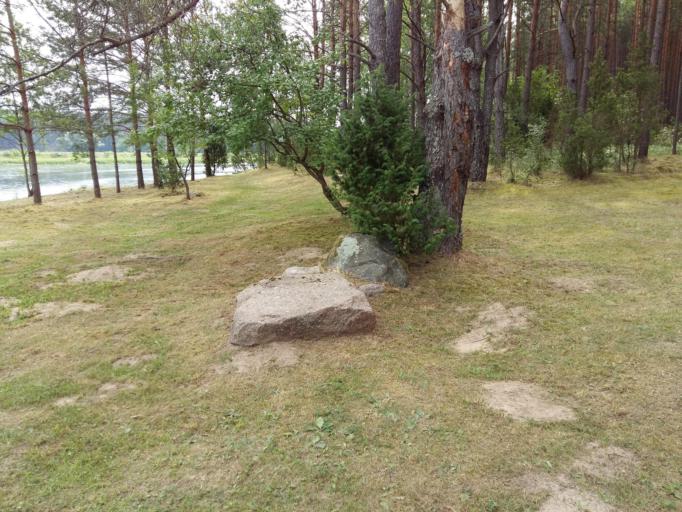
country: LT
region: Alytaus apskritis
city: Druskininkai
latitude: 54.1611
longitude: 24.1628
